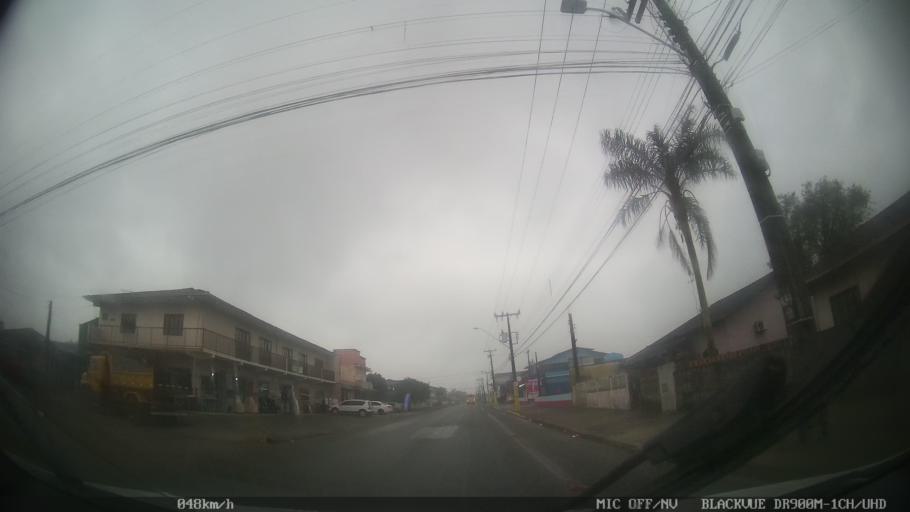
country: BR
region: Santa Catarina
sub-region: Joinville
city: Joinville
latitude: -26.2094
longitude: -48.8268
